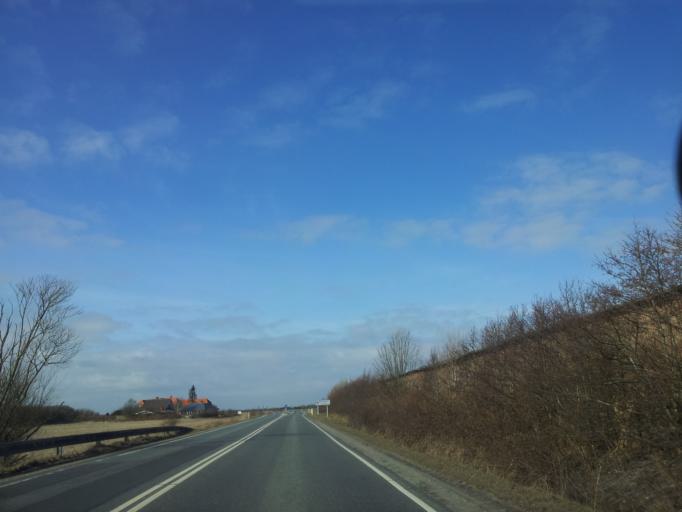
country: DK
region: South Denmark
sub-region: Esbjerg Kommune
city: Ribe
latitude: 55.3256
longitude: 8.7541
